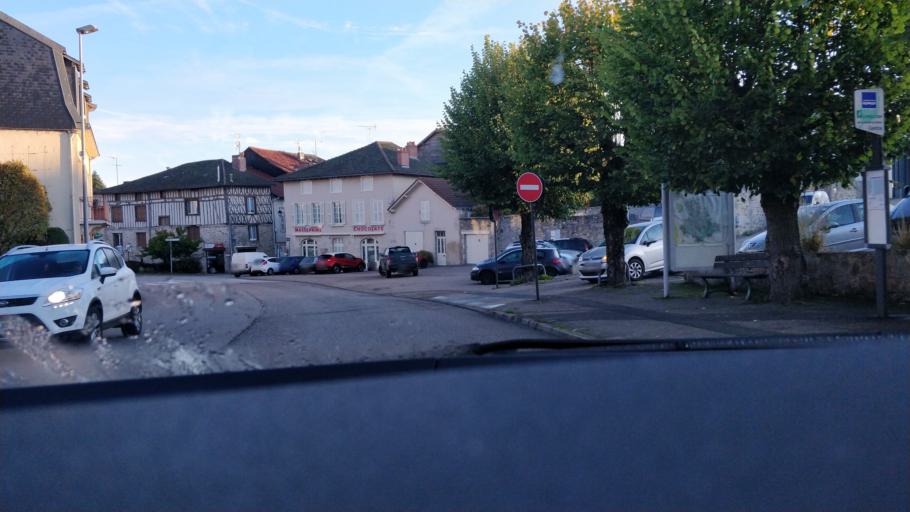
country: FR
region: Limousin
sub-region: Departement de la Haute-Vienne
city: Saint-Leonard-de-Noblat
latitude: 45.8379
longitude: 1.4922
